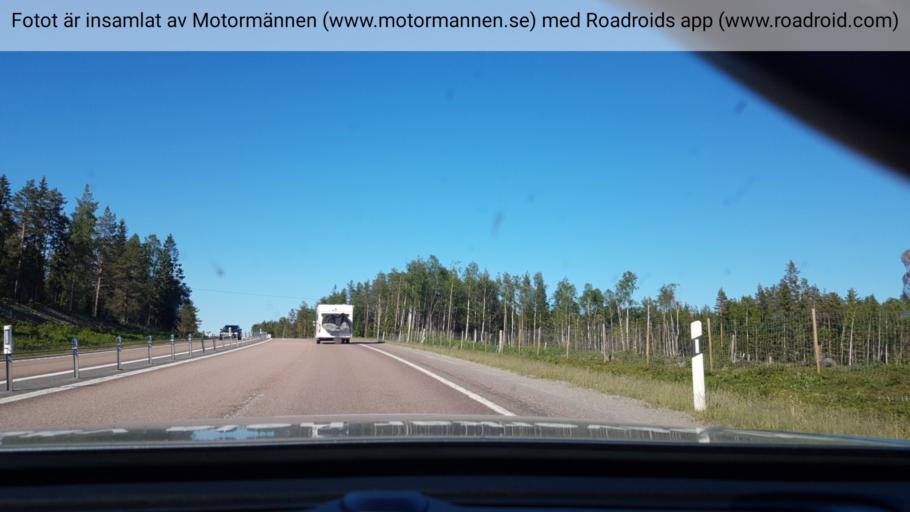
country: SE
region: Vaesternorrland
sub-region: Haernoesands Kommun
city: Haernoesand
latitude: 62.5645
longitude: 17.7308
